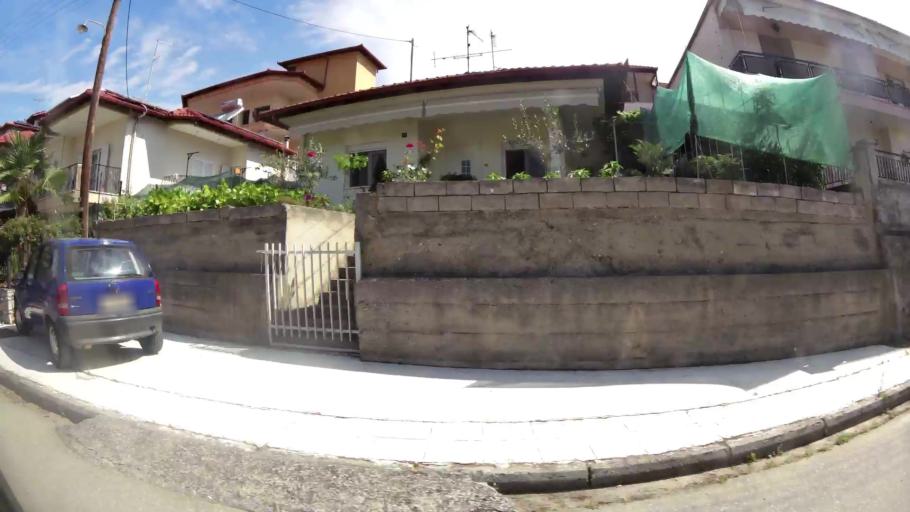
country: GR
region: Central Macedonia
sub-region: Nomos Pierias
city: Svoronos
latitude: 40.2755
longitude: 22.4843
